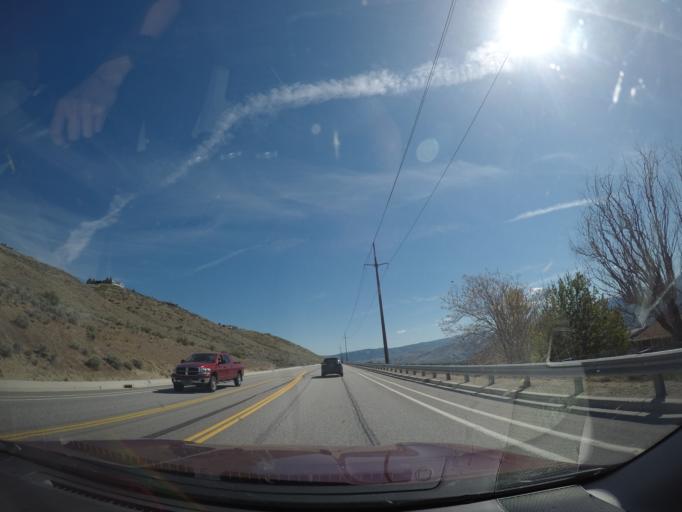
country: US
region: Washington
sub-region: Douglas County
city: East Wenatchee Bench
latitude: 47.4521
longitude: -120.2894
